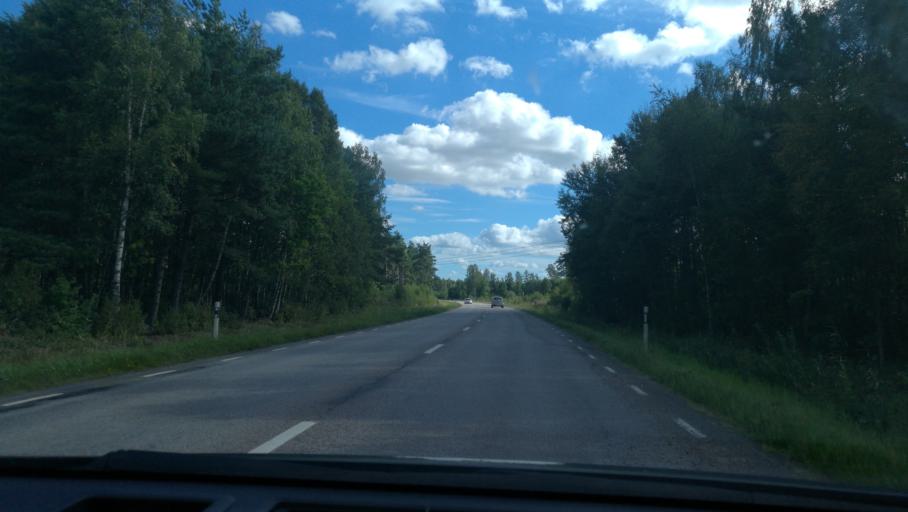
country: SE
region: Vaestra Goetaland
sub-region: Lidkopings Kommun
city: Vinninga
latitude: 58.4920
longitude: 13.2702
